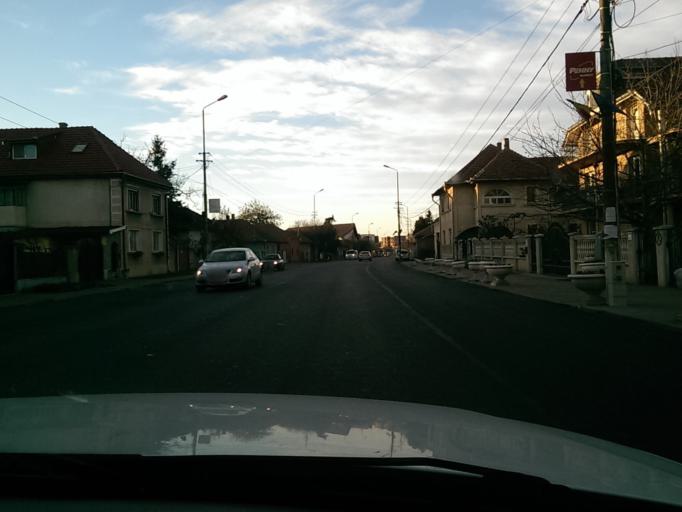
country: RO
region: Bihor
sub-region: Comuna Sanmartin
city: Sanmartin
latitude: 47.0051
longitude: 21.9754
